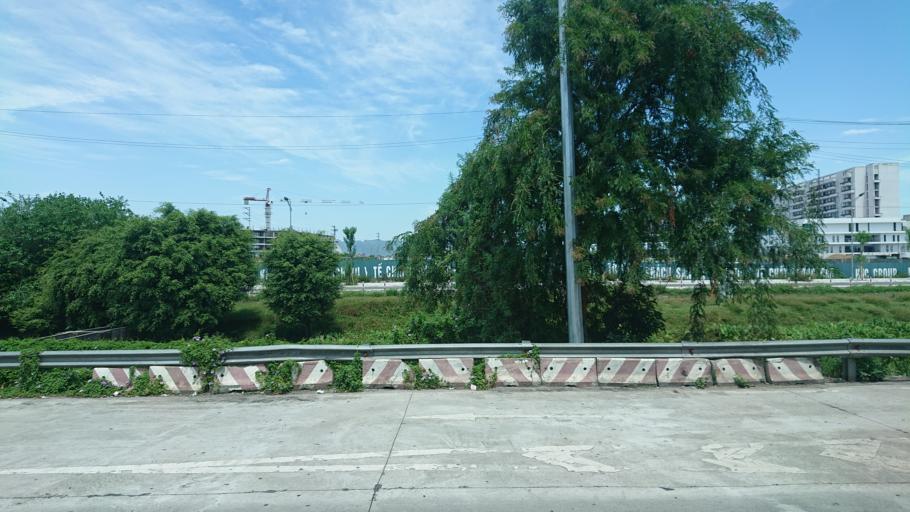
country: VN
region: Ha Nam
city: Thanh Pho Phu Ly
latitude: 20.5399
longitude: 105.9475
